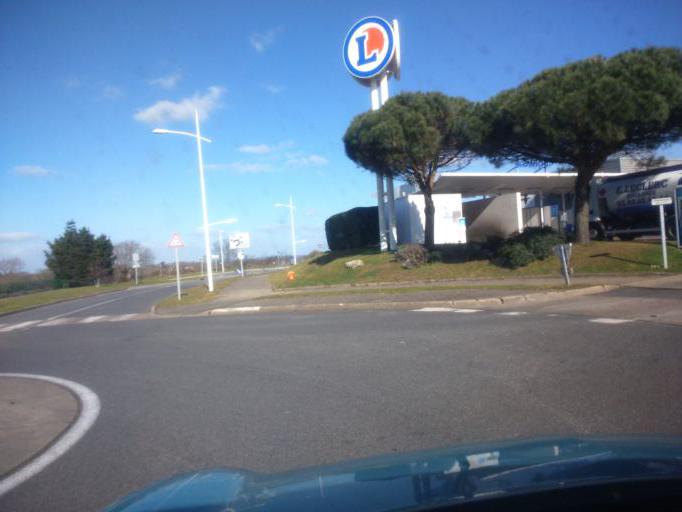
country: FR
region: Pays de la Loire
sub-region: Departement de la Loire-Atlantique
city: Guerande
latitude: 47.3292
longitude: -2.4126
